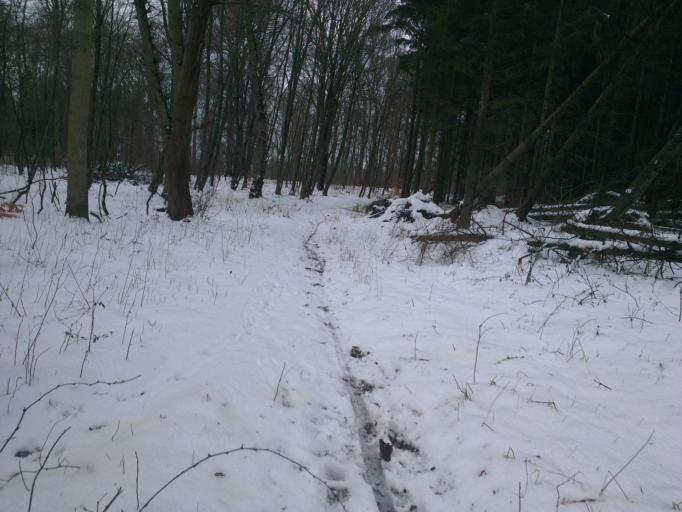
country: DK
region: Capital Region
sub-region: Frederikssund Kommune
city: Jaegerspris
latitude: 55.8496
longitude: 12.0137
